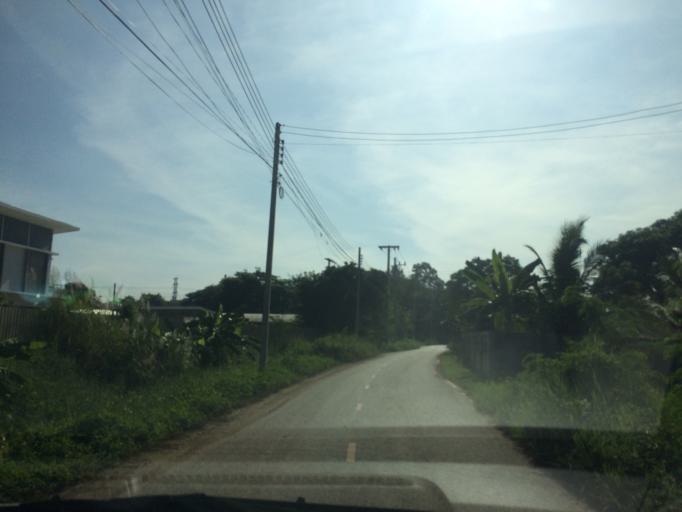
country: TH
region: Chiang Mai
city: Saraphi
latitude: 18.7285
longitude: 99.0117
